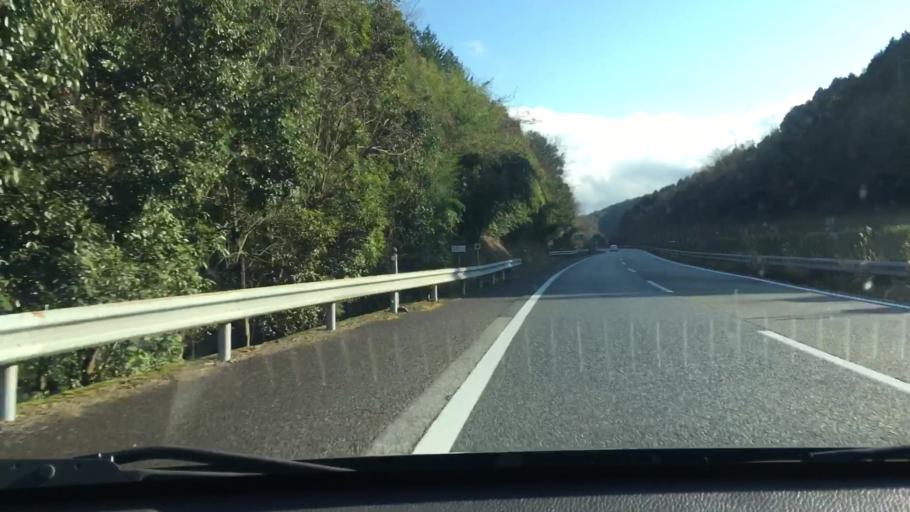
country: JP
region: Kumamoto
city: Hitoyoshi
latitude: 32.1750
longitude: 130.7896
